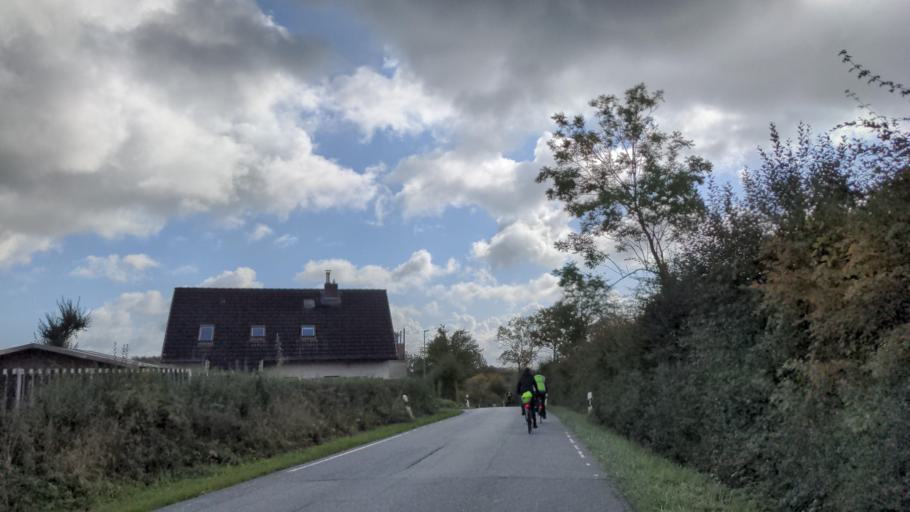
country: DE
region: Schleswig-Holstein
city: Reinfeld
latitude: 53.8405
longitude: 10.4741
